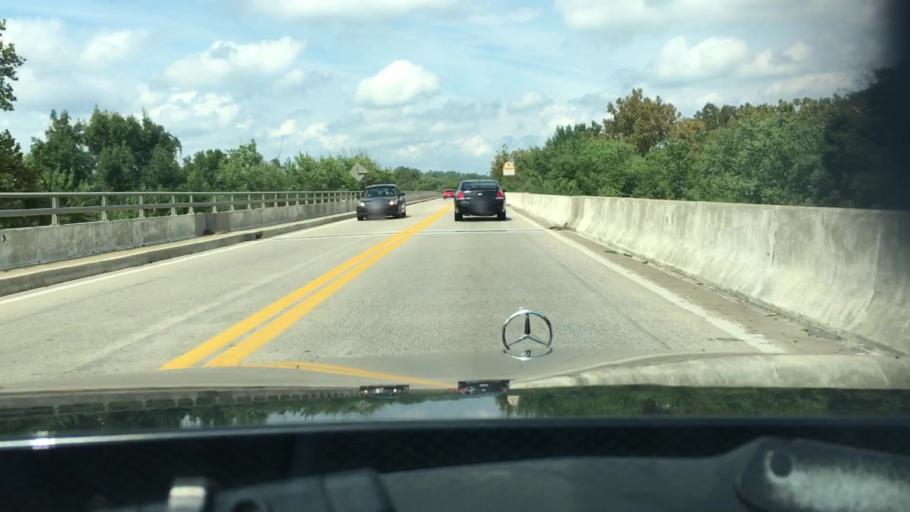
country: US
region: Maryland
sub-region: Washington County
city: Hancock
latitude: 39.6924
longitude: -78.1862
